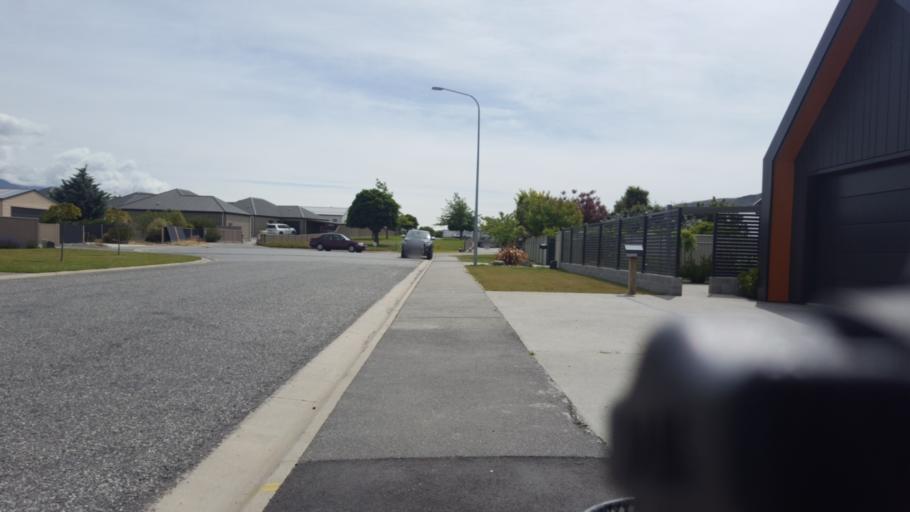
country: NZ
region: Otago
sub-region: Queenstown-Lakes District
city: Wanaka
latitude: -45.0517
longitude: 169.1966
